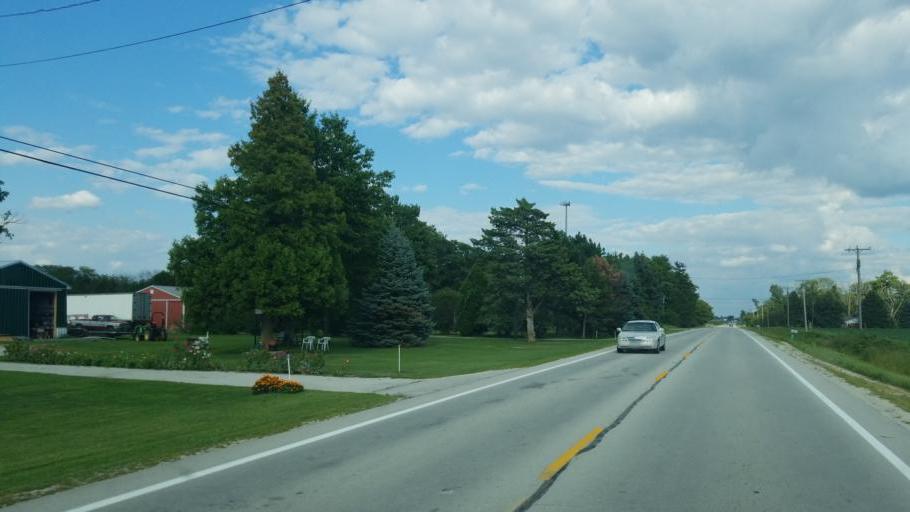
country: US
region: Ohio
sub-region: Sandusky County
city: Gibsonburg
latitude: 41.3413
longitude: -83.3743
